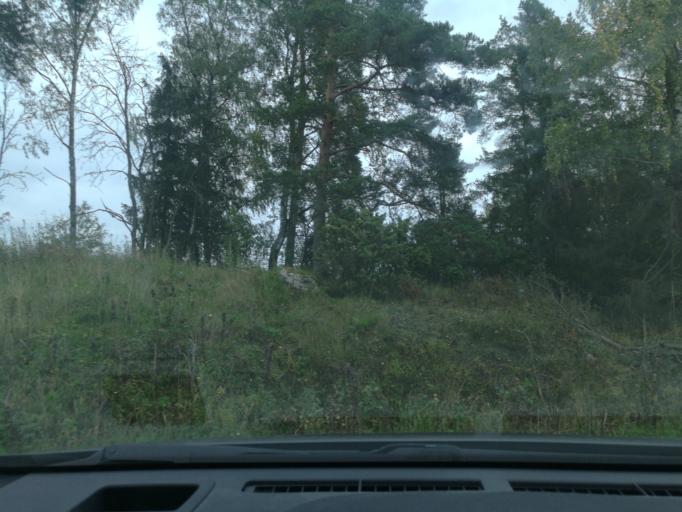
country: SE
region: Vaestmanland
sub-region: Vasteras
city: Tillberga
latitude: 59.7411
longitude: 16.6966
